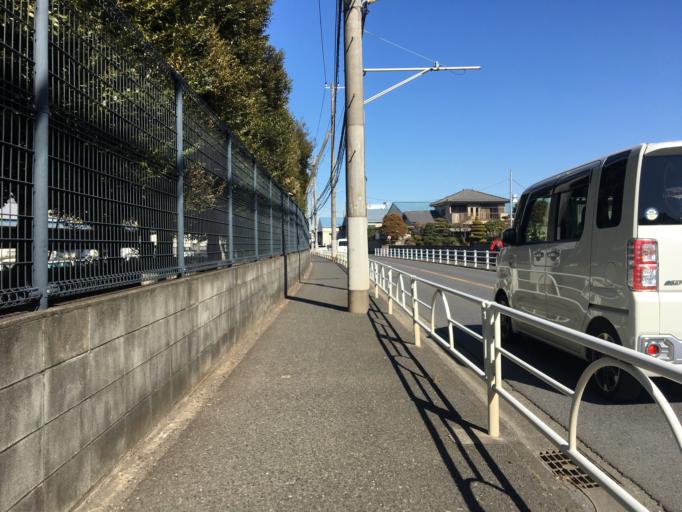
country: JP
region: Saitama
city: Asaka
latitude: 35.8028
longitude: 139.5753
